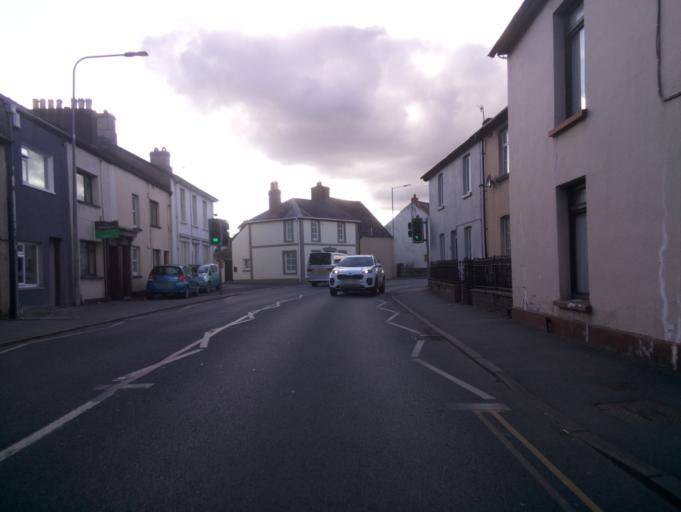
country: GB
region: Wales
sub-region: Sir Powys
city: Brecon
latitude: 51.9459
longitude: -3.3988
